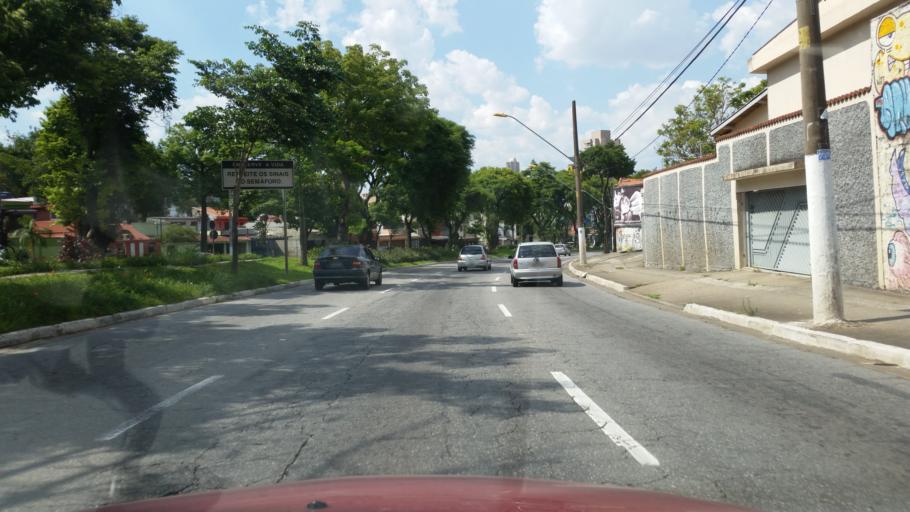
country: BR
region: Sao Paulo
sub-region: Santo Andre
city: Santo Andre
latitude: -23.6522
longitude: -46.5486
